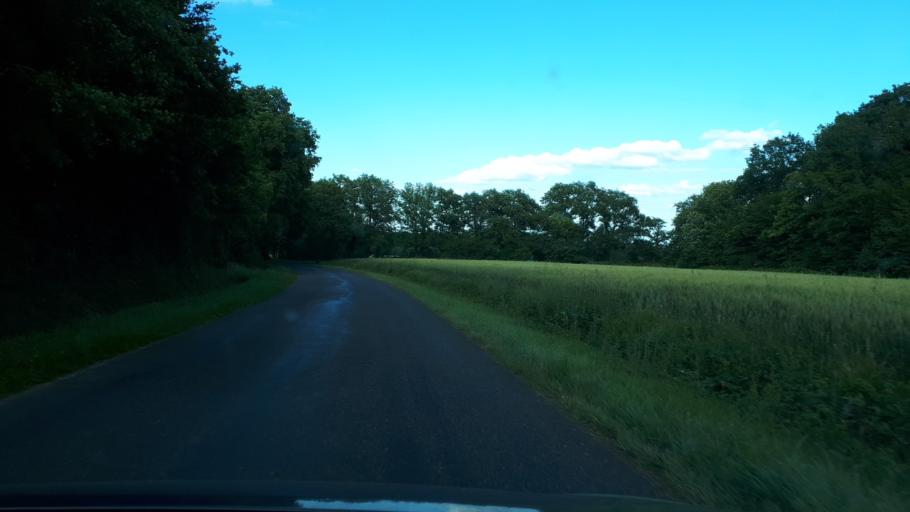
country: FR
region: Centre
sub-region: Departement du Loir-et-Cher
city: Sarge-sur-Braye
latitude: 47.9276
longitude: 0.9015
